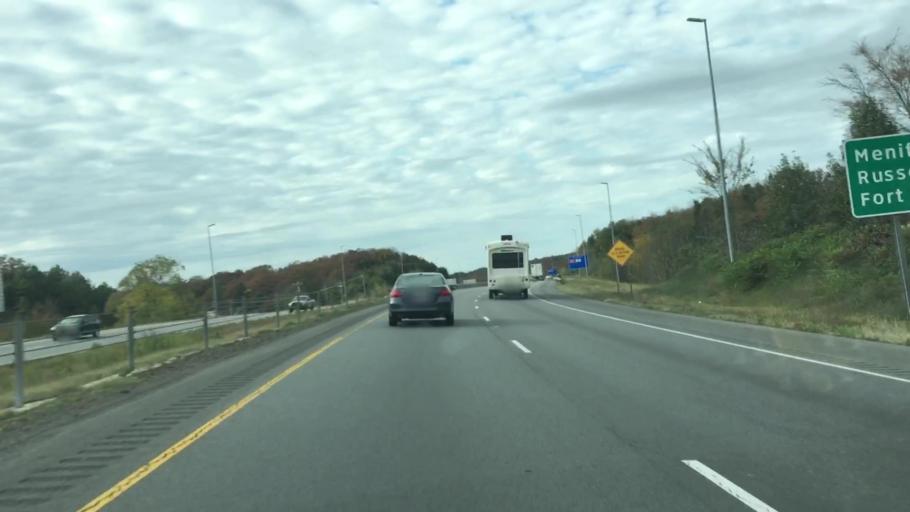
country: US
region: Arkansas
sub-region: Faulkner County
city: Conway
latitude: 35.1145
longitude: -92.4463
